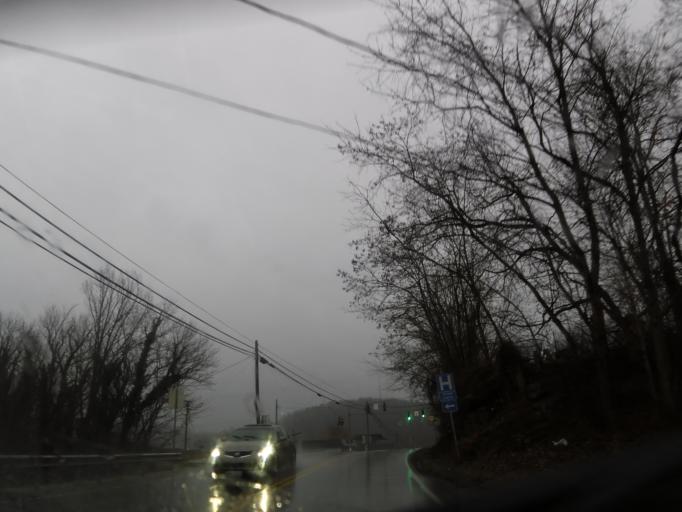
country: US
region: Kentucky
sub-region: Rockcastle County
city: Mount Vernon
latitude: 37.3532
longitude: -84.3414
